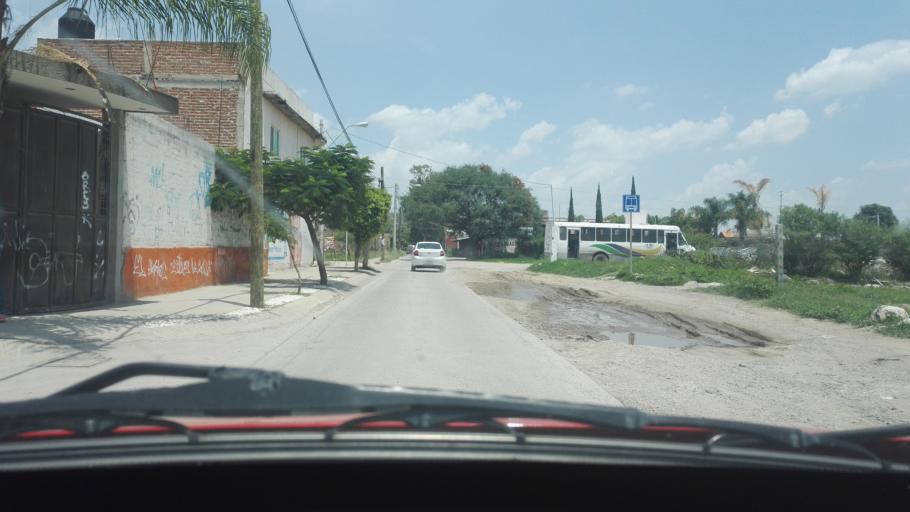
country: MX
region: Guanajuato
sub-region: Leon
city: Fraccionamiento Paraiso Real
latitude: 21.0701
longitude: -101.6068
